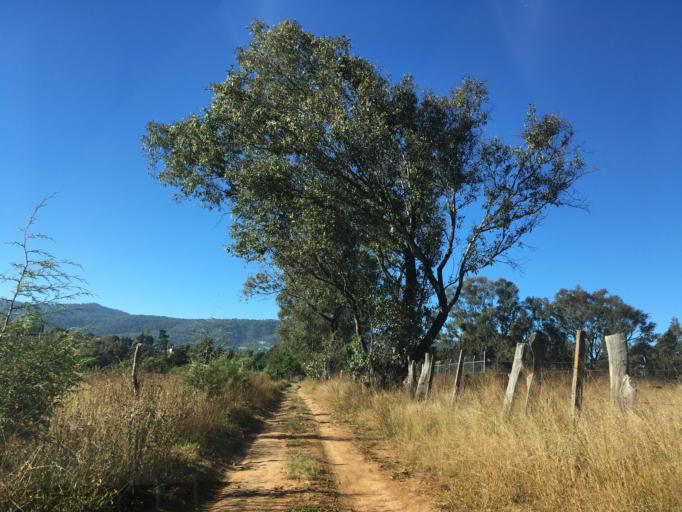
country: MX
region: Michoacan
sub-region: Morelia
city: Montana Monarca (Punta Altozano)
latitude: 19.6576
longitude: -101.1490
